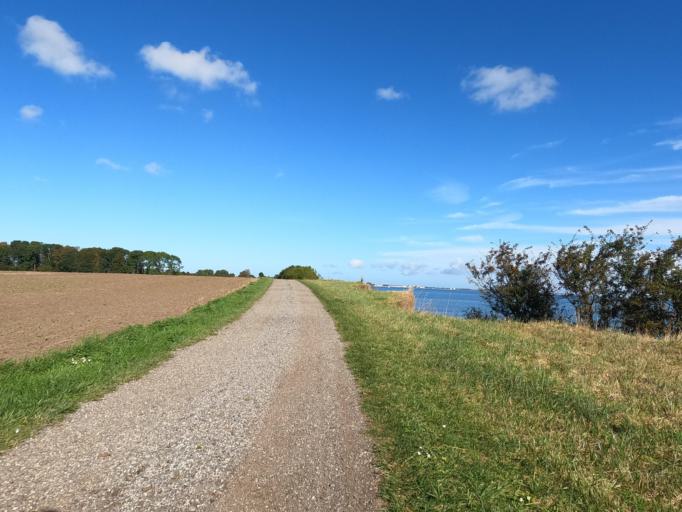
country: DE
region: Schleswig-Holstein
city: Neukirchen
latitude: 54.3152
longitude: 11.0740
